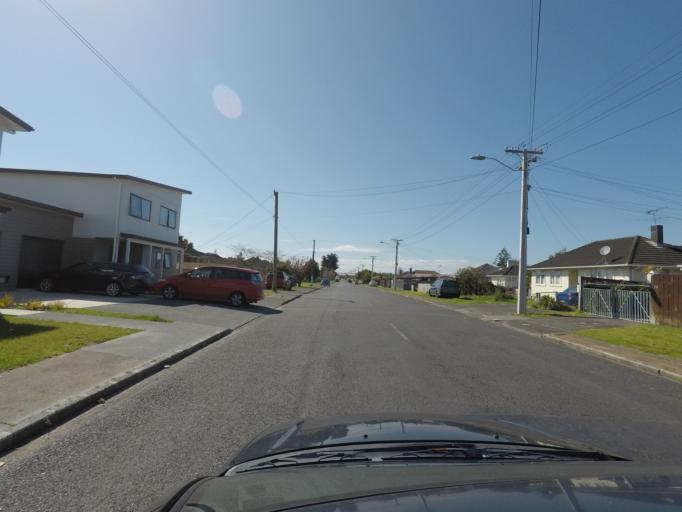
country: NZ
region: Auckland
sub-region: Auckland
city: Tamaki
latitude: -36.9283
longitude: 174.8549
